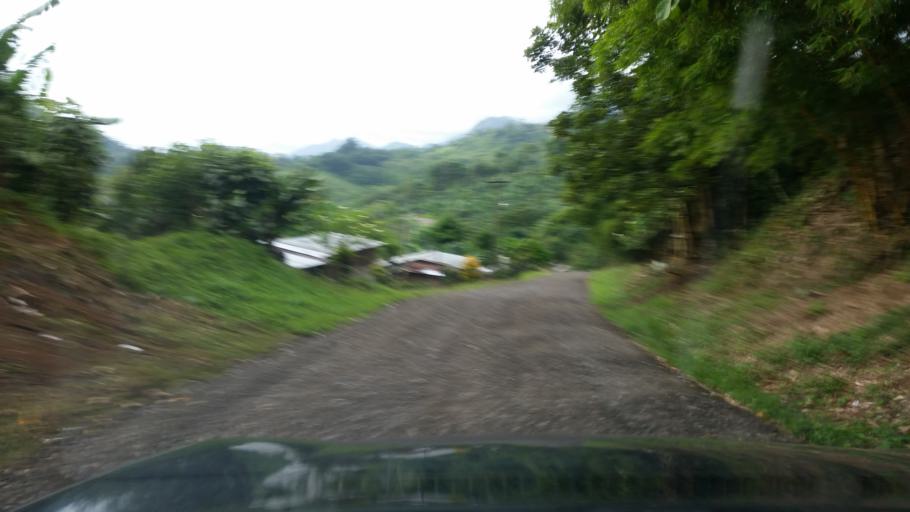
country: NI
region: Jinotega
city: Jinotega
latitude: 13.2531
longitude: -85.7374
